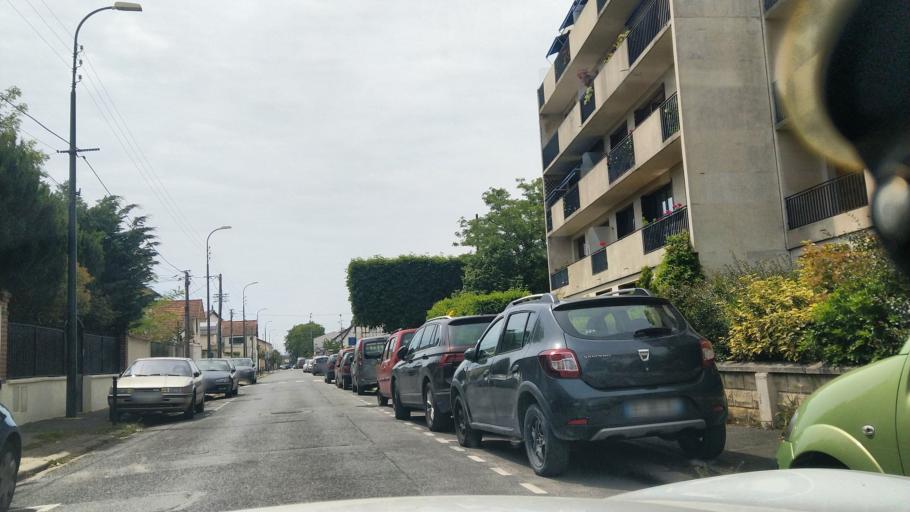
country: FR
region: Ile-de-France
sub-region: Departement du Val-de-Marne
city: Saint-Maur-des-Fosses
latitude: 48.8026
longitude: 2.5086
